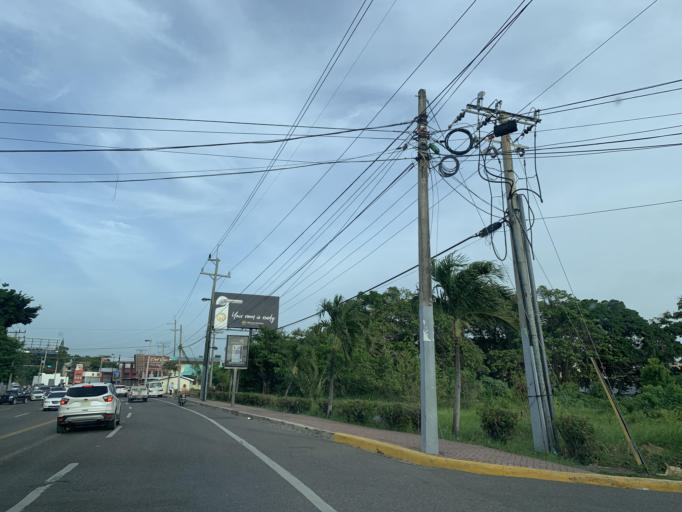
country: DO
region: Puerto Plata
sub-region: Puerto Plata
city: Puerto Plata
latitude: 19.7775
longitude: -70.6672
